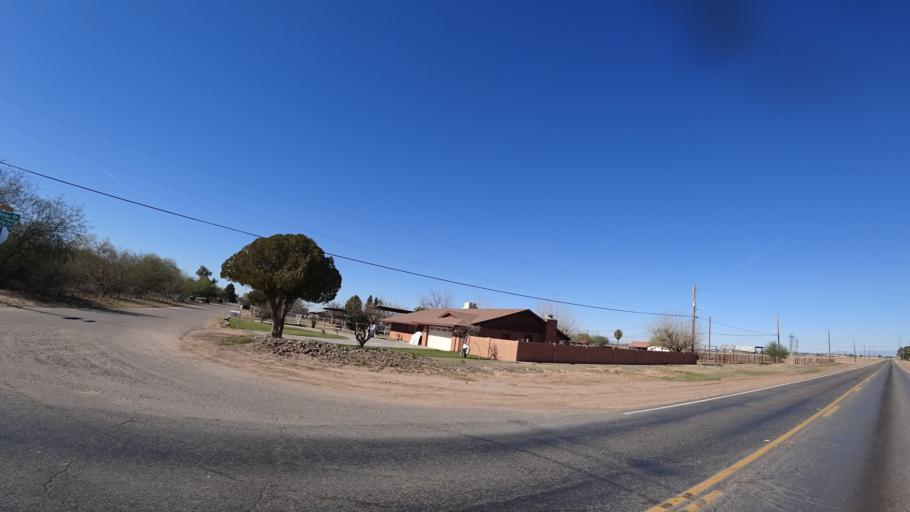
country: US
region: Arizona
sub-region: Maricopa County
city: Avondale
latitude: 33.3936
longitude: -112.3233
